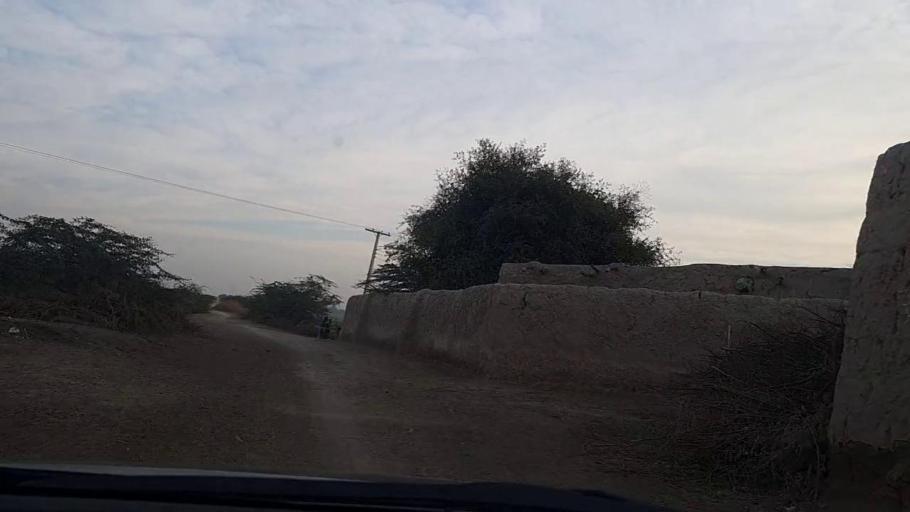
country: PK
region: Sindh
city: Sakrand
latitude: 26.1929
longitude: 68.3344
